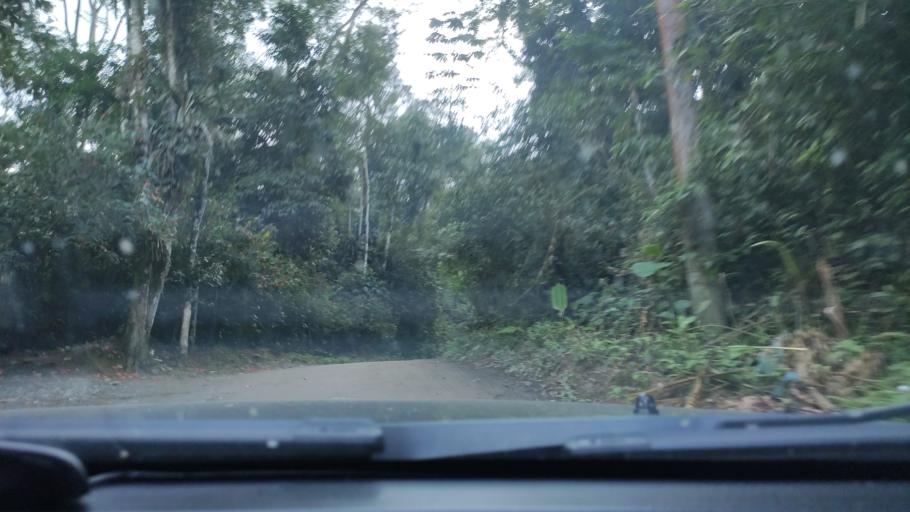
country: BR
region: Sao Paulo
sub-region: Sao Sebastiao
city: Sao Sebastiao
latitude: -23.7143
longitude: -45.4924
